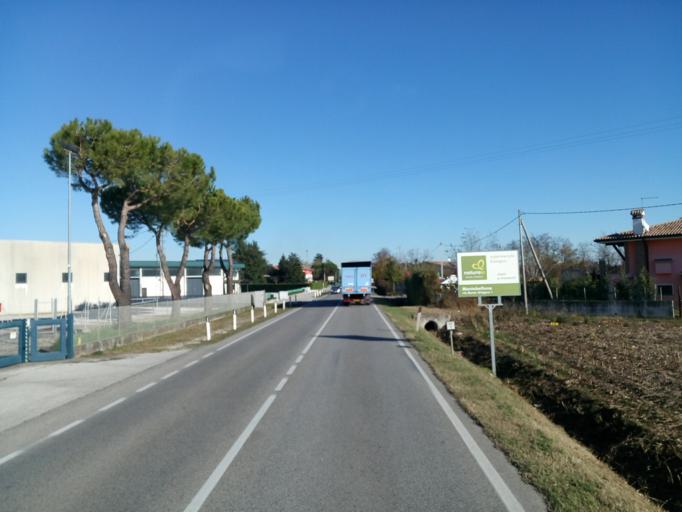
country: IT
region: Veneto
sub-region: Provincia di Treviso
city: Altivole
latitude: 45.7377
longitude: 11.9644
